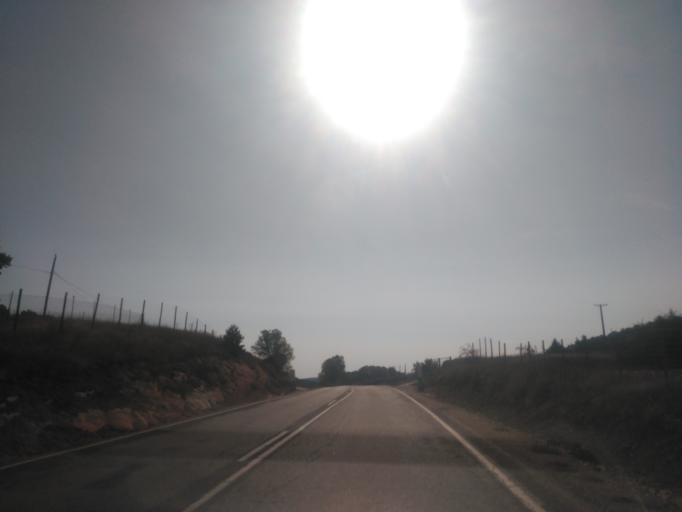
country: ES
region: Castille and Leon
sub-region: Provincia de Soria
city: Casarejos
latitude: 41.8049
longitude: -3.0493
